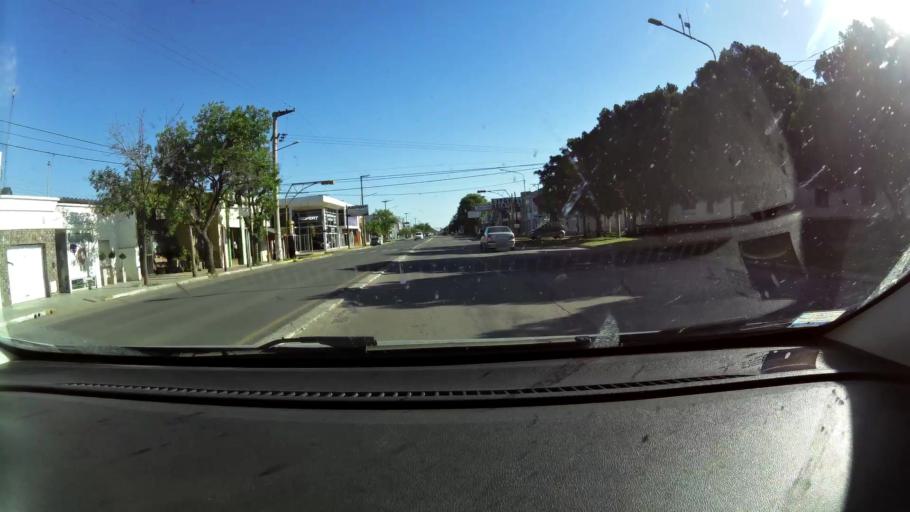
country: AR
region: Cordoba
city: San Francisco
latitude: -31.4191
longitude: -62.0950
